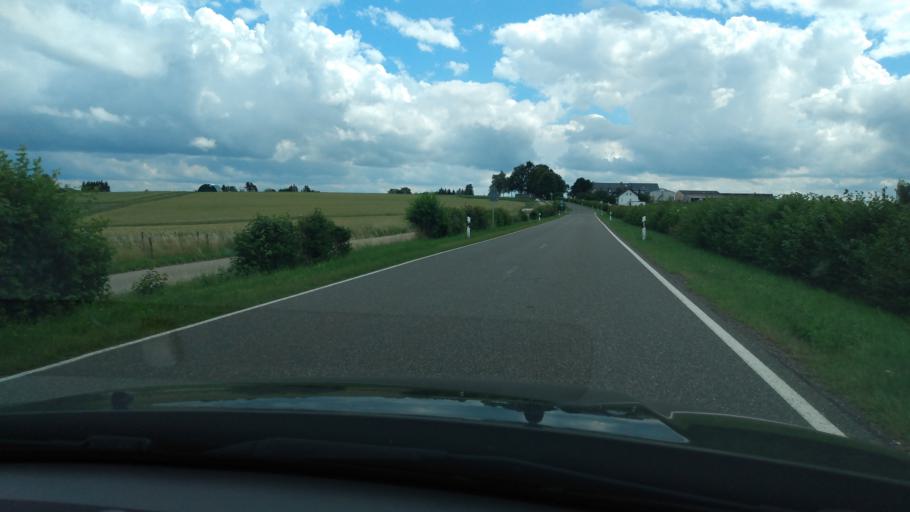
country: DE
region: Rheinland-Pfalz
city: Manderscheid
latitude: 50.0990
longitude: 6.8002
